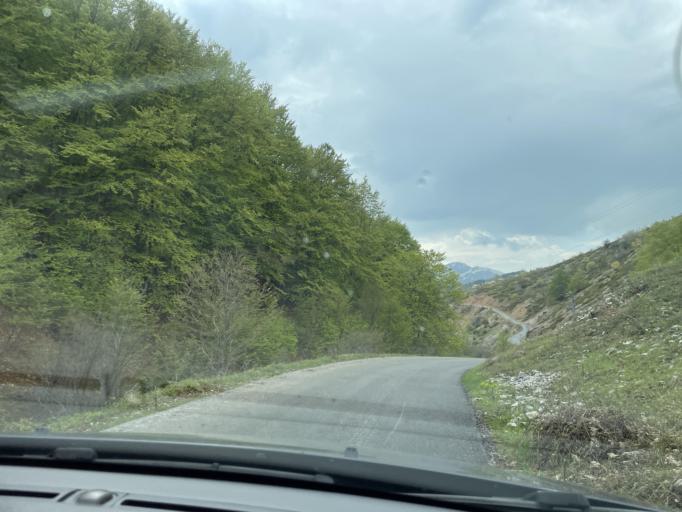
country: MK
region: Opstina Rostusa
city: Rostusha
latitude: 41.5934
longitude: 20.6671
